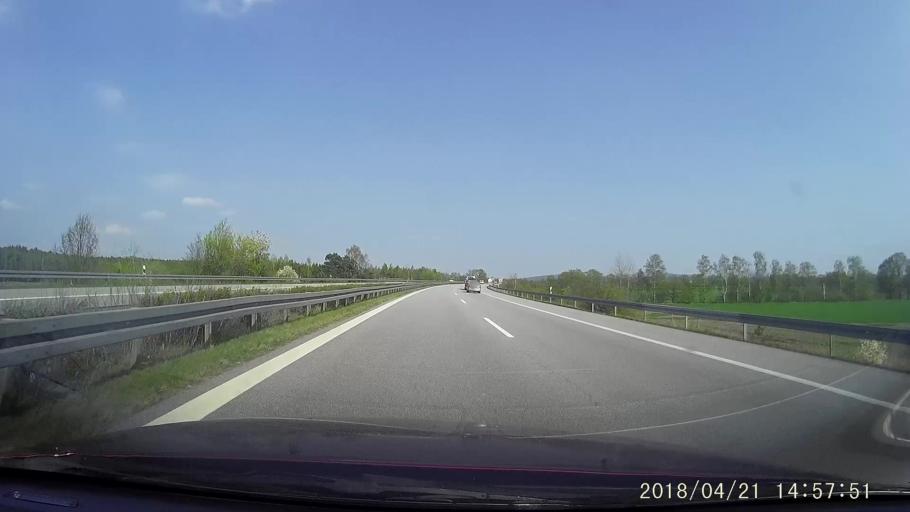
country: DE
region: Saxony
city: Weissenberg
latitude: 51.2135
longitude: 14.7172
